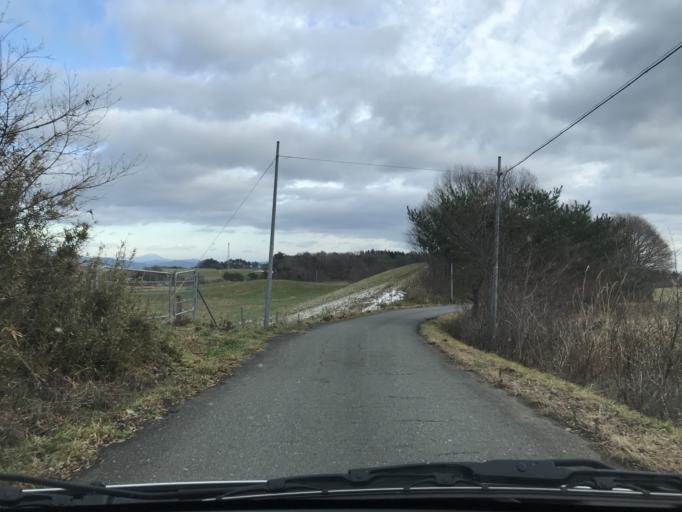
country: JP
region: Iwate
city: Ichinoseki
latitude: 38.9776
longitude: 141.0213
